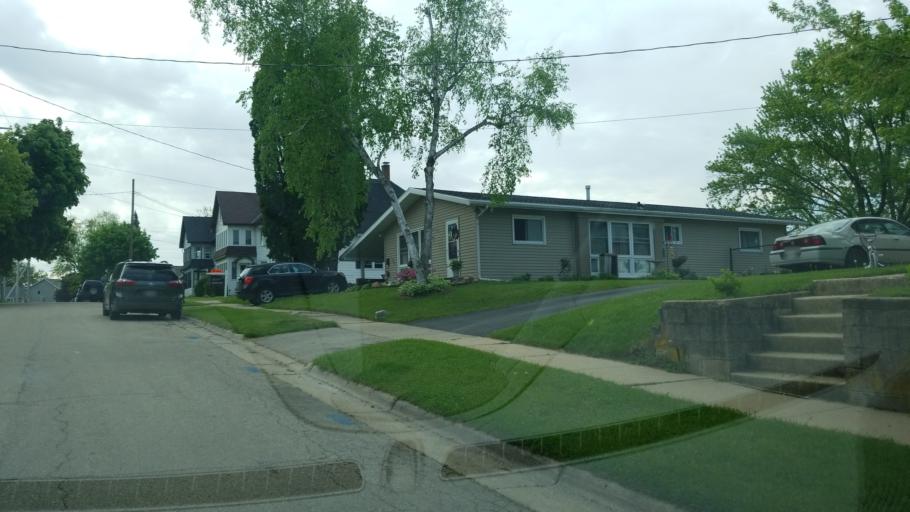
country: US
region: Wisconsin
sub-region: Dane County
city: Stoughton
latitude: 42.9147
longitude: -89.2075
